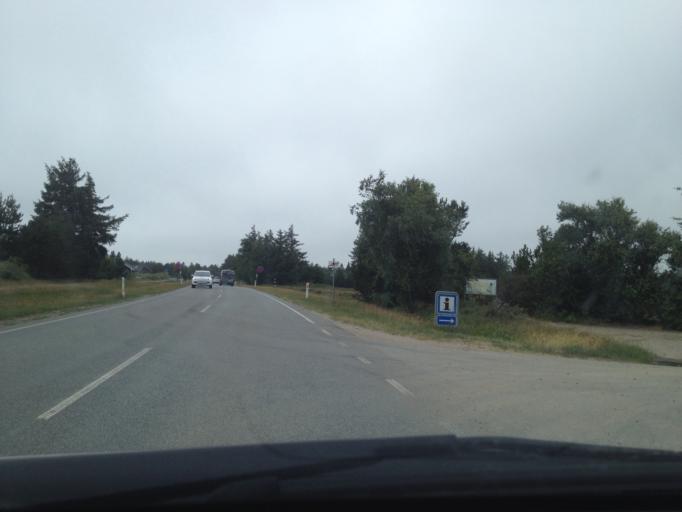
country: DK
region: South Denmark
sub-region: Varde Kommune
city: Oksbol
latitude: 55.5633
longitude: 8.1708
